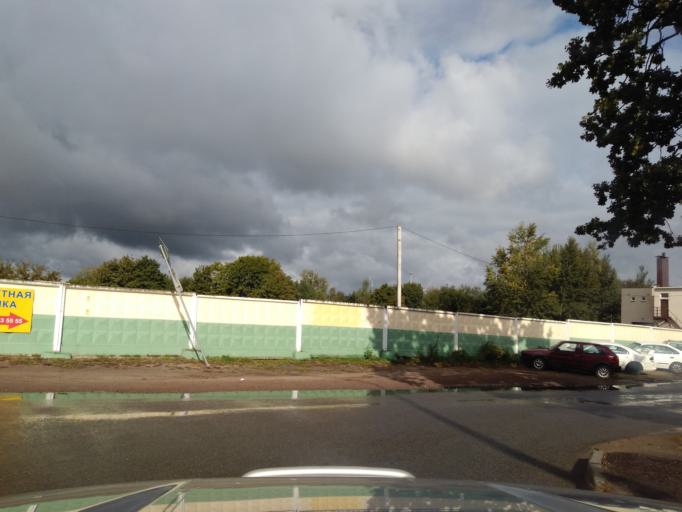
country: BY
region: Minsk
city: Novoye Medvezhino
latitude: 53.9018
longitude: 27.4203
